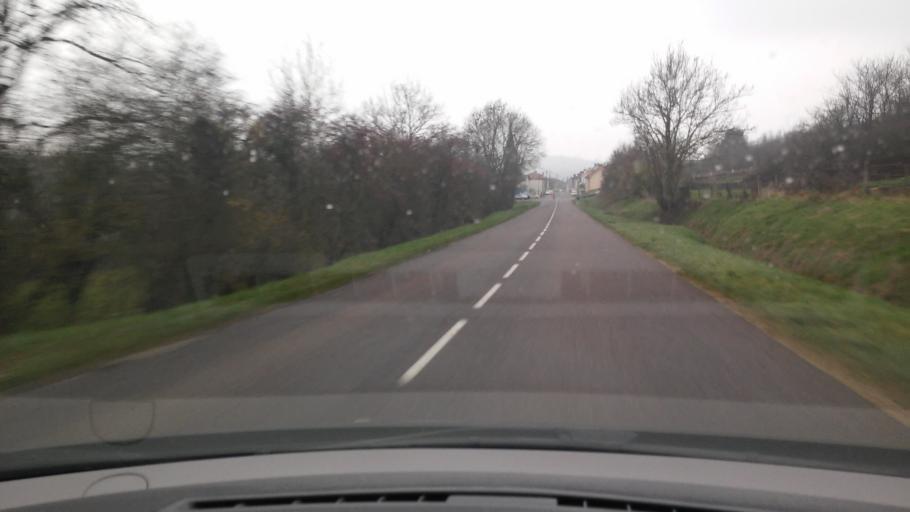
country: FR
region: Lorraine
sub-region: Departement de la Moselle
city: Courcelles-Chaussy
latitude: 49.1013
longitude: 6.4860
